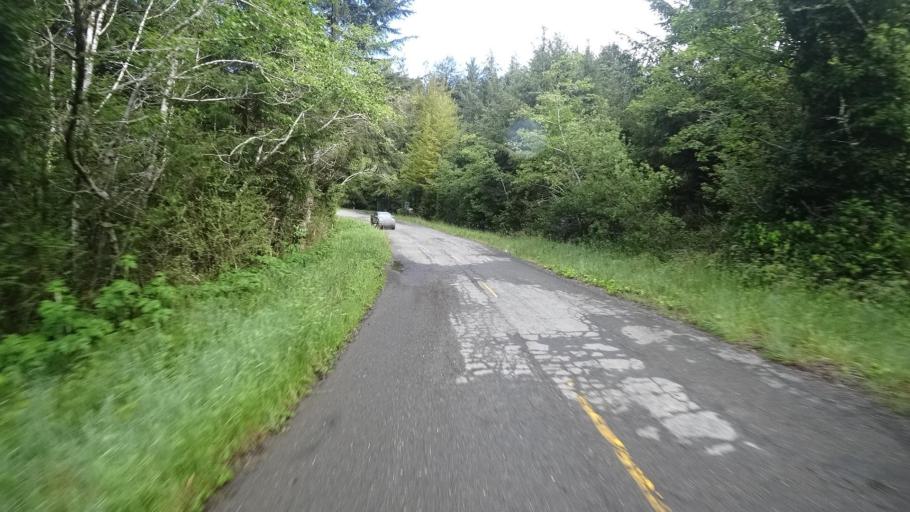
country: US
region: California
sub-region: Humboldt County
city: Westhaven-Moonstone
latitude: 41.0471
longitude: -124.1143
